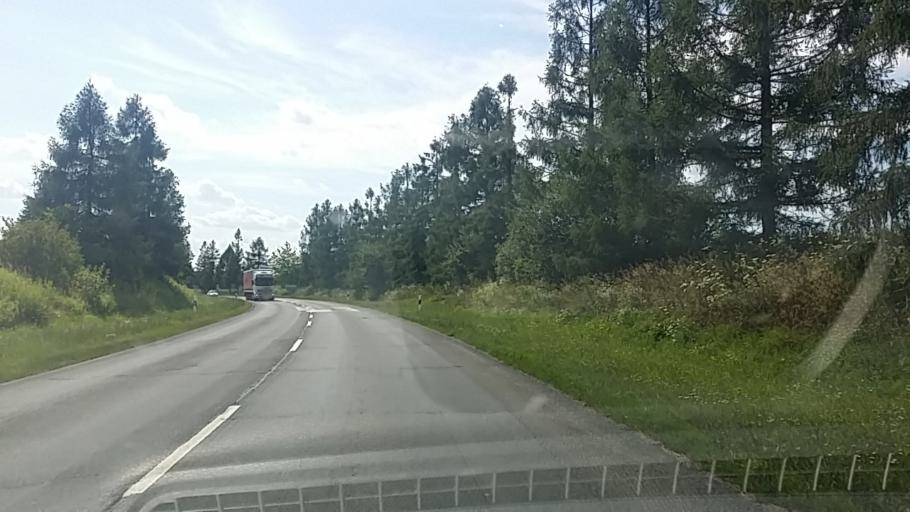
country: HU
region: Zala
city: Nagykanizsa
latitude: 46.4664
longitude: 17.0134
